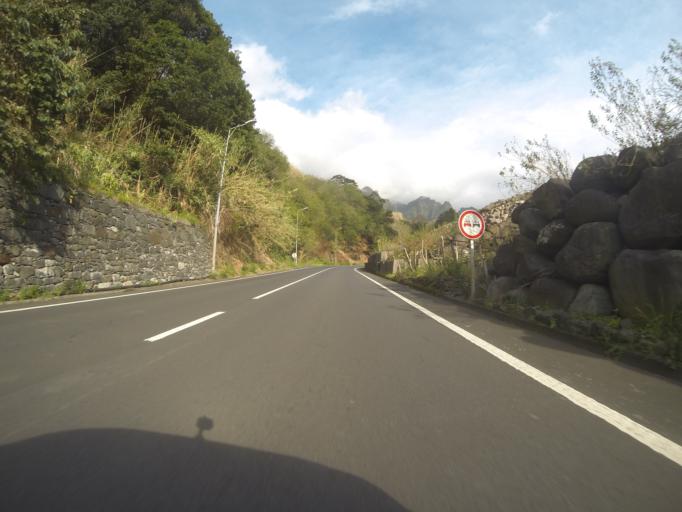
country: PT
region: Madeira
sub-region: Sao Vicente
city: Sao Vicente
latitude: 32.7897
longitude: -17.0303
